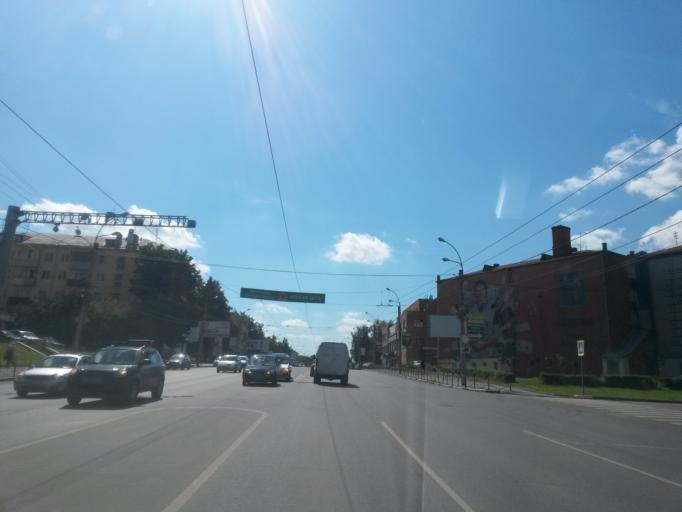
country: RU
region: Ivanovo
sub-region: Gorod Ivanovo
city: Ivanovo
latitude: 57.0024
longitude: 40.9891
